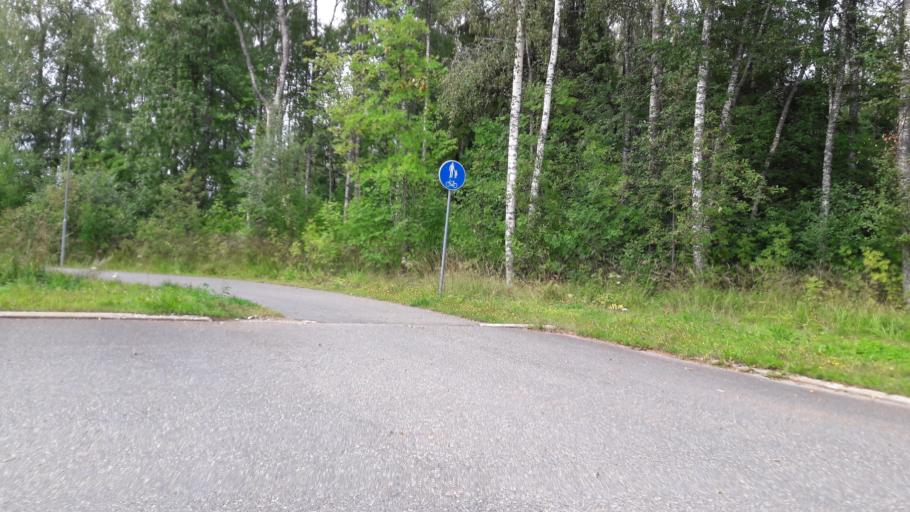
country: FI
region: North Karelia
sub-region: Joensuu
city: Joensuu
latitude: 62.5761
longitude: 29.7772
